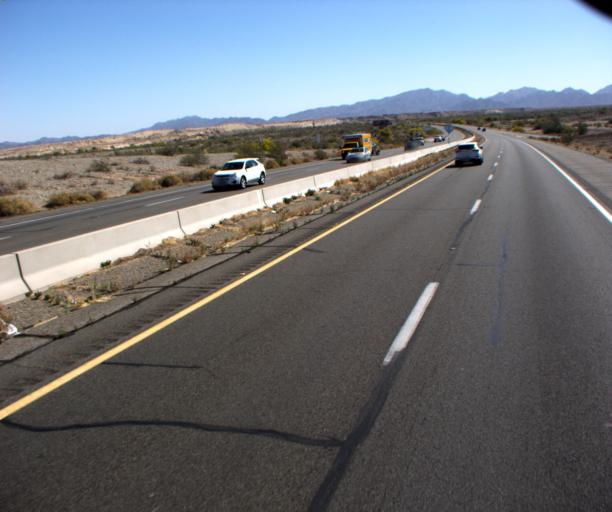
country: US
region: Arizona
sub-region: La Paz County
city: Ehrenberg
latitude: 33.6024
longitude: -114.5183
